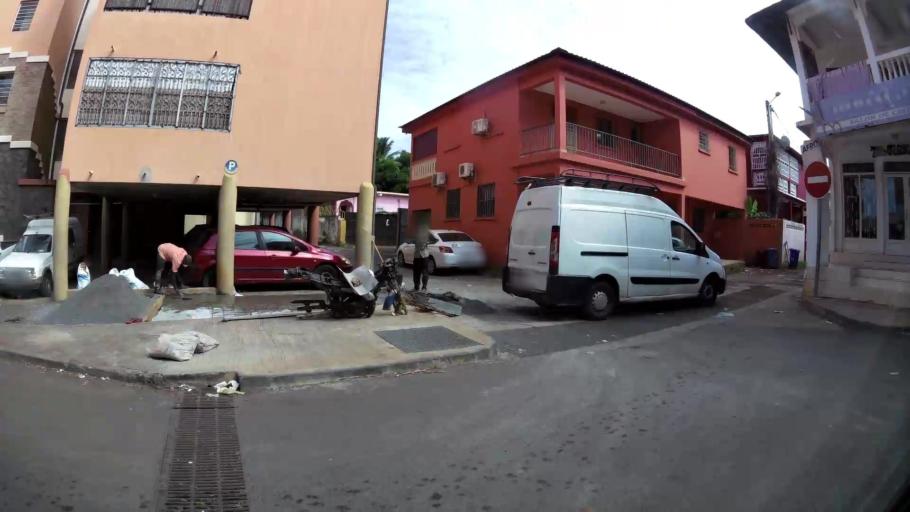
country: YT
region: Mamoudzou
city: Mamoudzou
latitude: -12.7828
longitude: 45.2289
